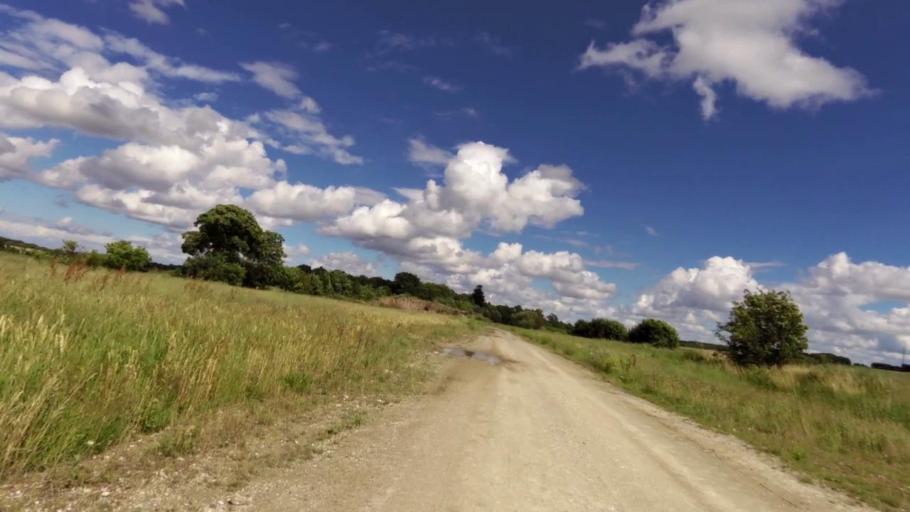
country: PL
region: Pomeranian Voivodeship
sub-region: Powiat slupski
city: Ustka
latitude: 54.5161
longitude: 16.7278
